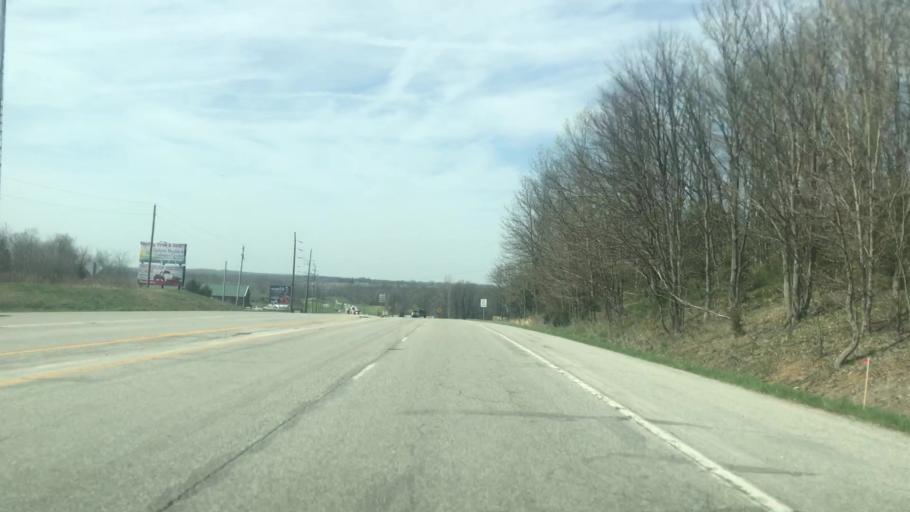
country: US
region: Indiana
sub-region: Putnam County
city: Cloverdale
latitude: 39.5369
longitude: -86.8035
